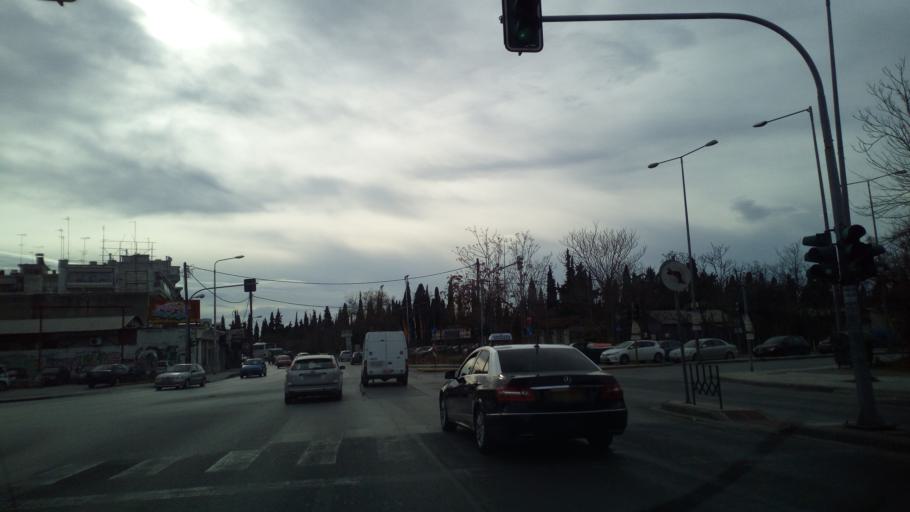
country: GR
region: Central Macedonia
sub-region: Nomos Thessalonikis
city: Ampelokipoi
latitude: 40.6571
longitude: 22.9346
